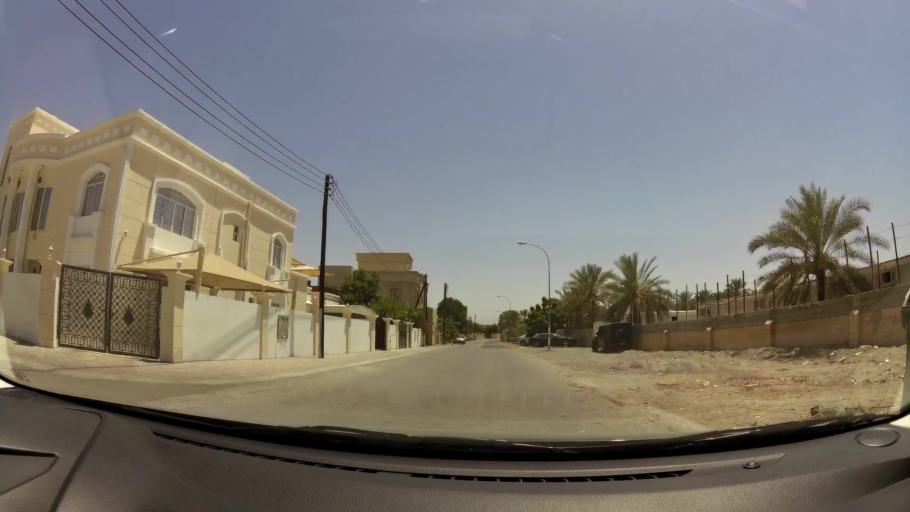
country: OM
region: Muhafazat Masqat
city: As Sib al Jadidah
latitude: 23.6224
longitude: 58.2326
